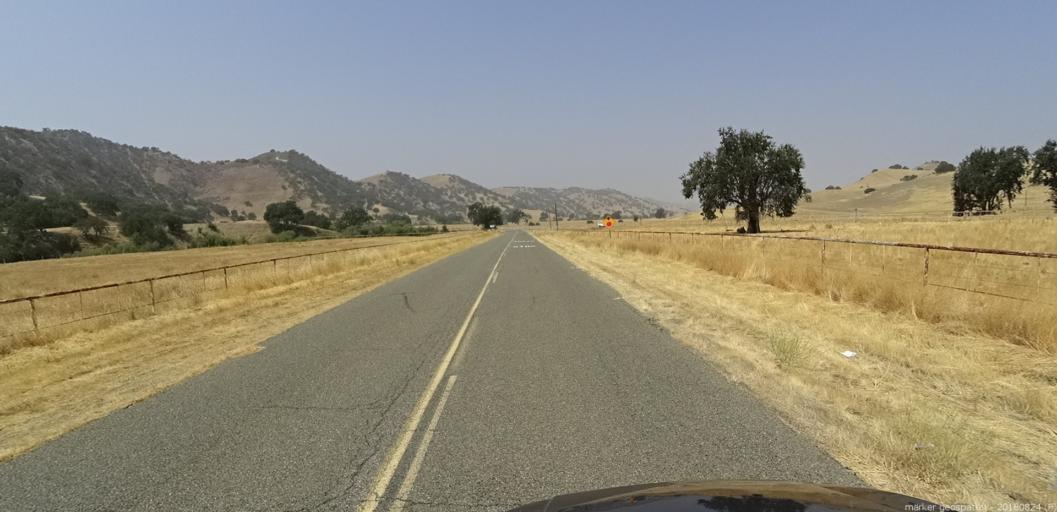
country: US
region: California
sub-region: Monterey County
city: King City
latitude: 36.1869
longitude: -120.8182
